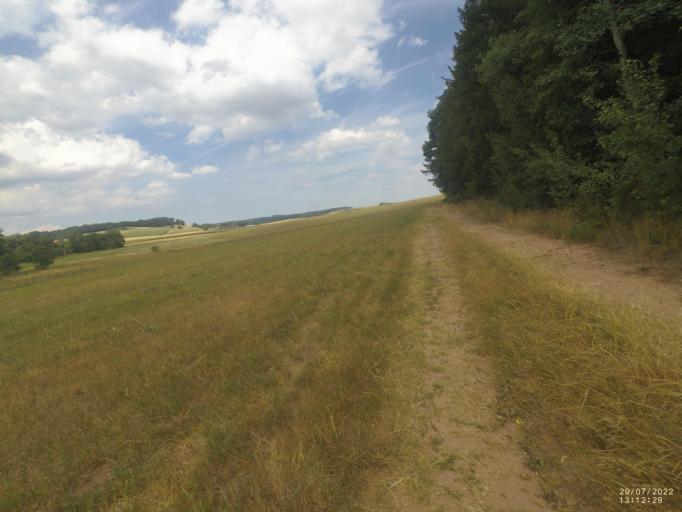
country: DE
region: Rheinland-Pfalz
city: Steffeln
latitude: 50.2756
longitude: 6.5771
